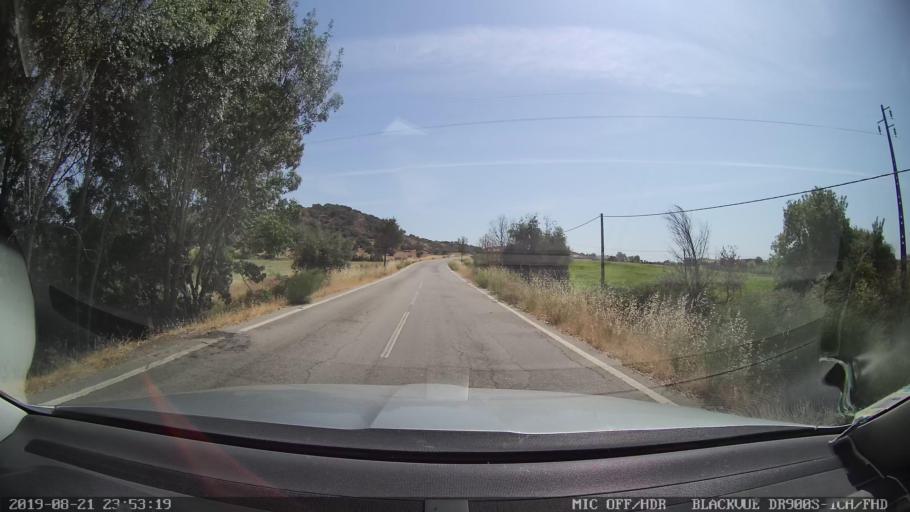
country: PT
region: Castelo Branco
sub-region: Idanha-A-Nova
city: Idanha-a-Nova
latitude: 39.9095
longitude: -7.2160
